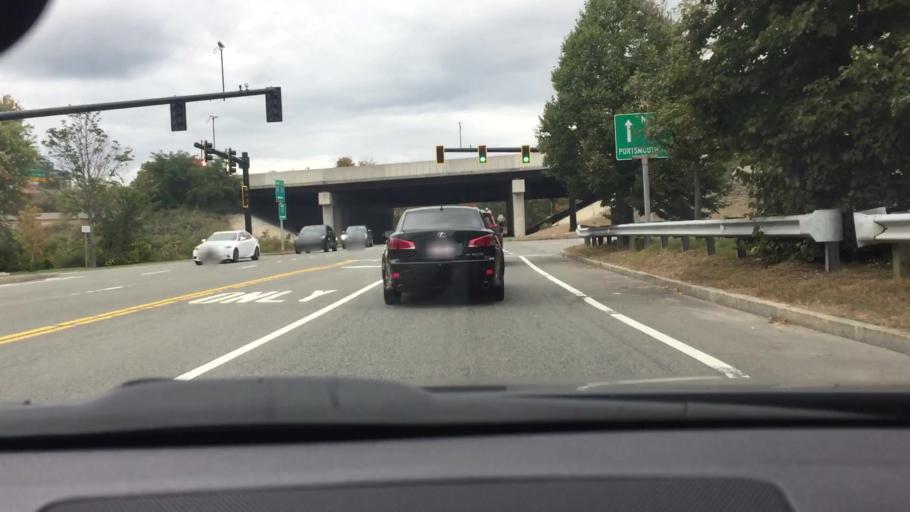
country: US
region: Massachusetts
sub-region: Norfolk County
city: Dedham
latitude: 42.2118
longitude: -71.1494
